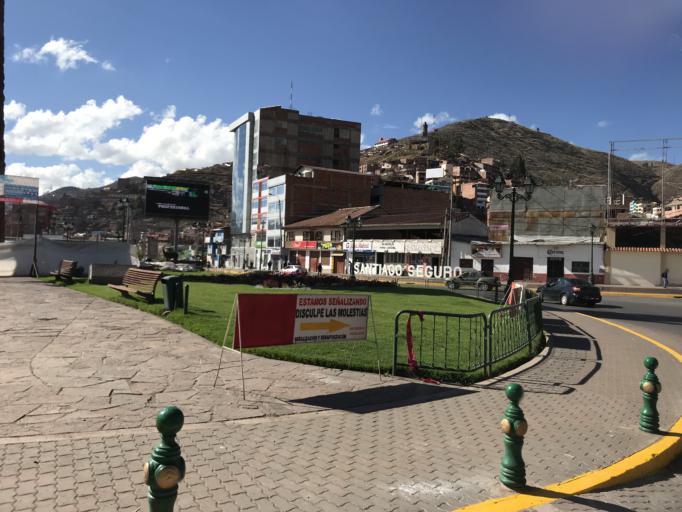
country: PE
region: Cusco
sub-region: Provincia de Cusco
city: Cusco
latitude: -13.5315
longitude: -71.9687
